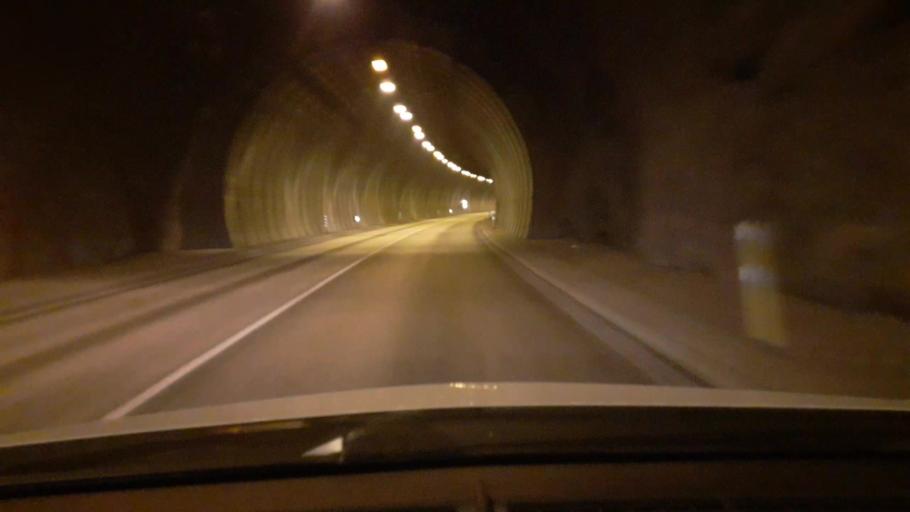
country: IS
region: Capital Region
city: Reykjavik
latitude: 64.2841
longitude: -21.8440
